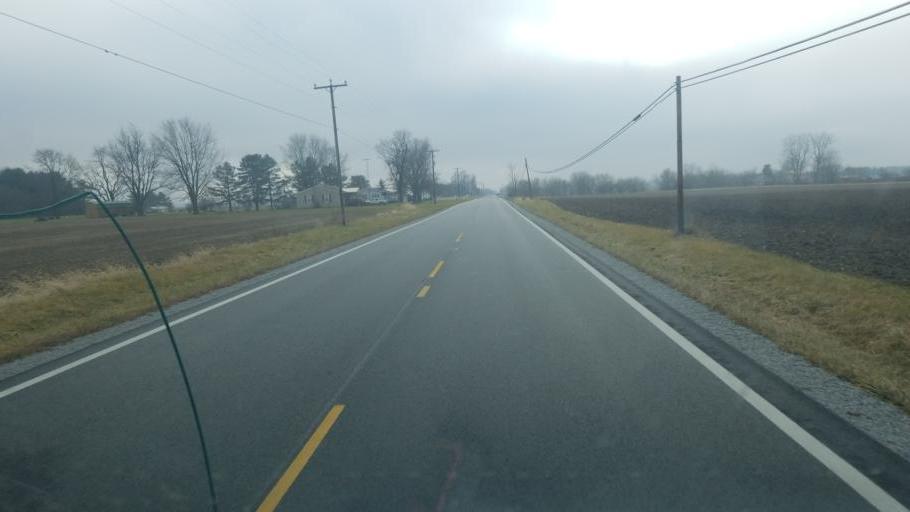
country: US
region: Ohio
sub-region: Hardin County
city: Kenton
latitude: 40.6761
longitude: -83.5248
